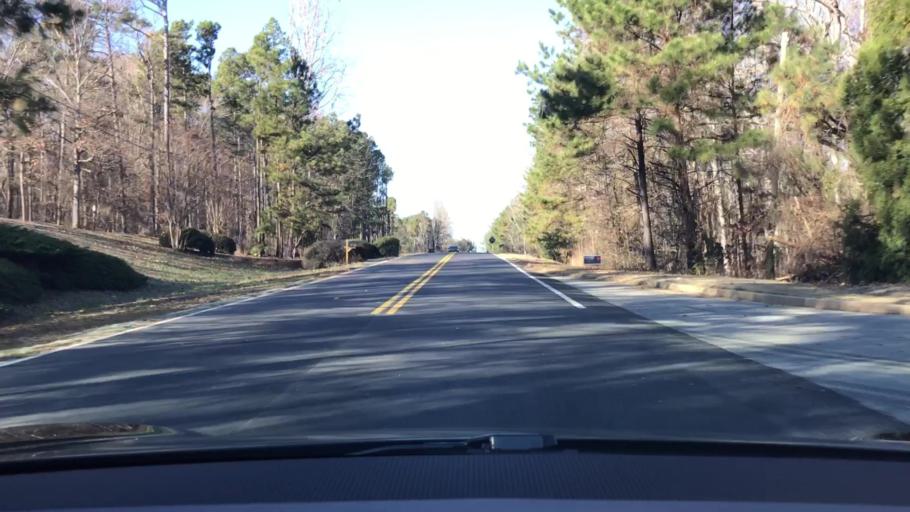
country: US
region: Georgia
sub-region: Barrow County
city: Auburn
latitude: 34.0866
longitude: -83.8688
